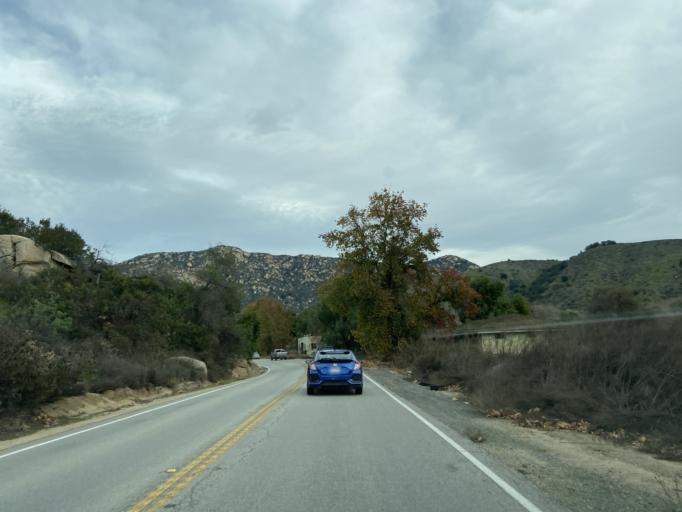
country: US
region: California
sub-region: San Diego County
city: Rainbow
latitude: 33.3442
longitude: -117.1228
